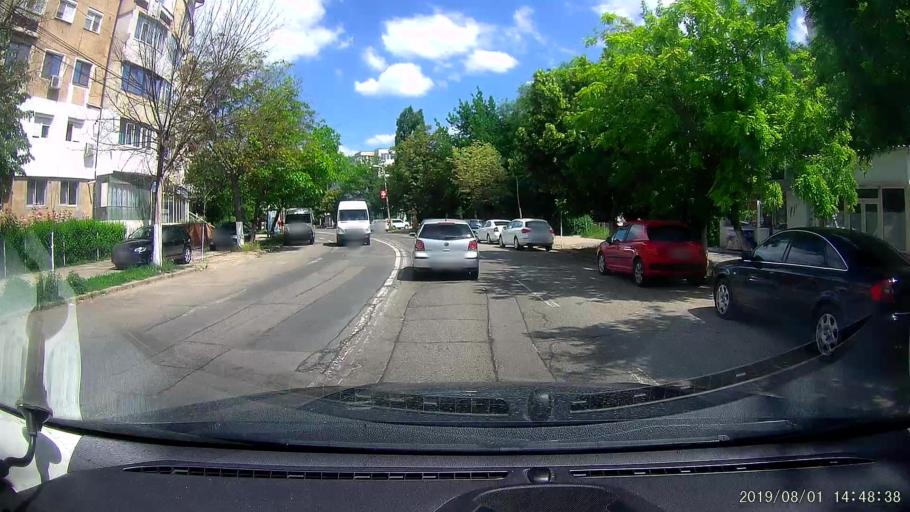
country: RO
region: Galati
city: Galati
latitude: 45.4094
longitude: 28.0105
